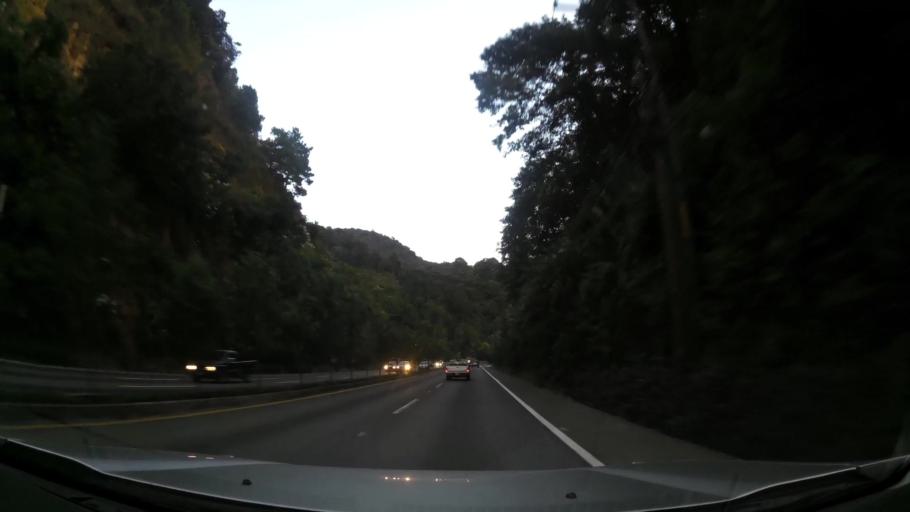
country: GT
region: Sacatepequez
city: San Lucas Sacatepequez
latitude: 14.6065
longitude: -90.6341
